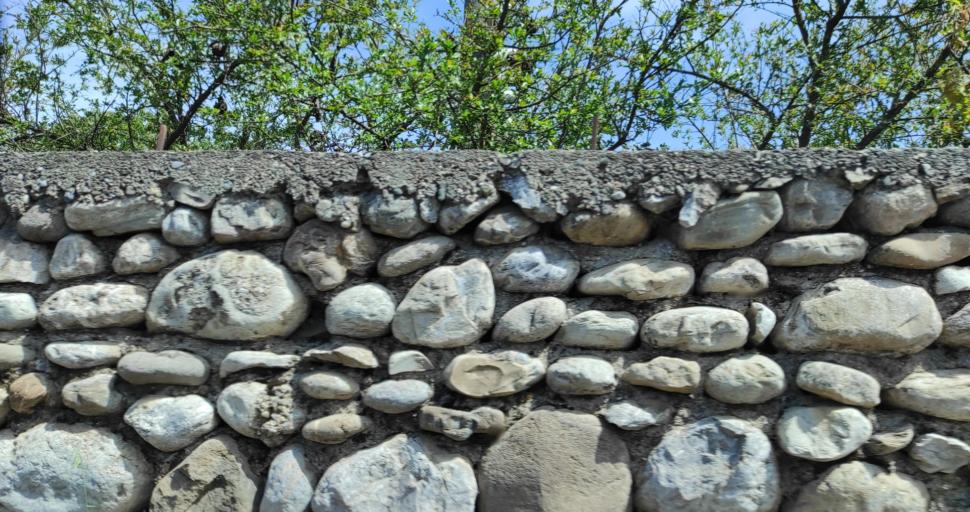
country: AL
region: Shkoder
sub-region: Rrethi i Malesia e Madhe
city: Gruemire
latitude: 42.1306
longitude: 19.5514
